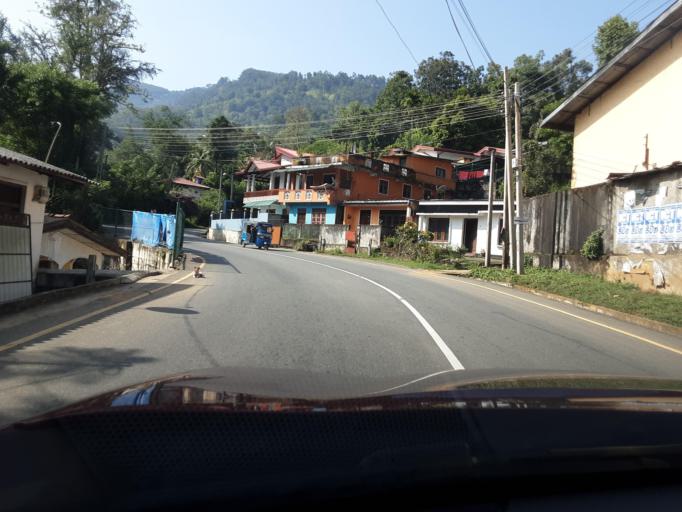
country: LK
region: Uva
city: Badulla
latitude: 6.9684
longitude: 81.0874
